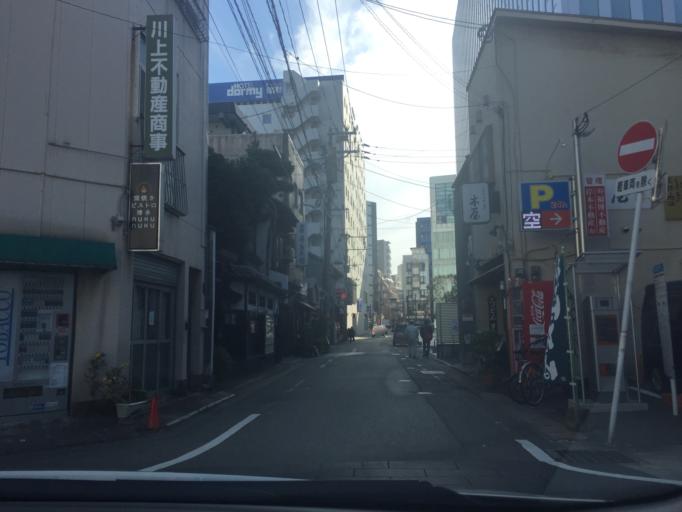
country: JP
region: Fukuoka
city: Fukuoka-shi
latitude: 33.5942
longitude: 130.4121
